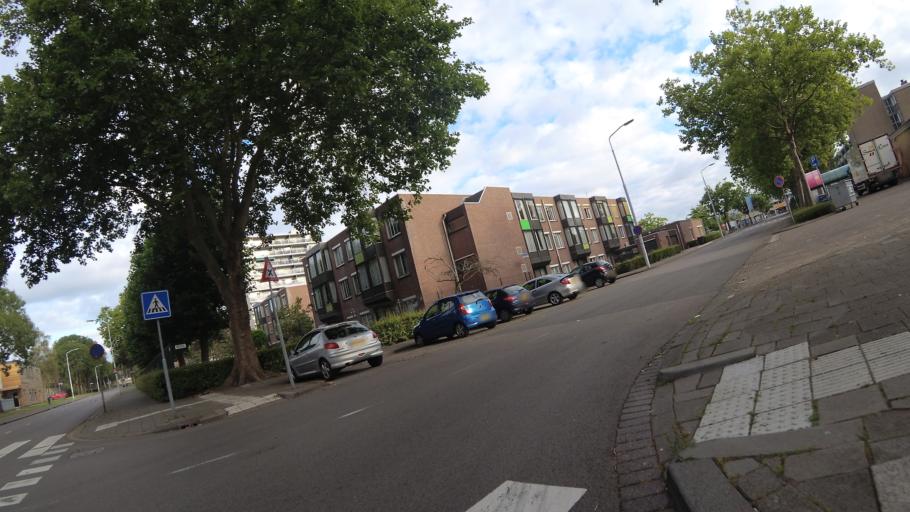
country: NL
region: North Brabant
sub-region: Gemeente Breda
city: Hoge Vucht
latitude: 51.6061
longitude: 4.7888
